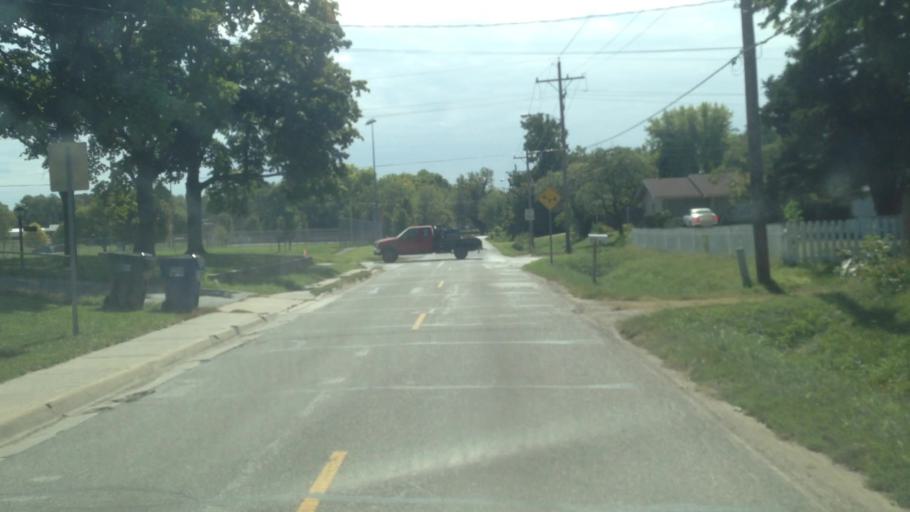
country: US
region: Kansas
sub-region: Douglas County
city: Lawrence
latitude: 38.9829
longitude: -95.2239
